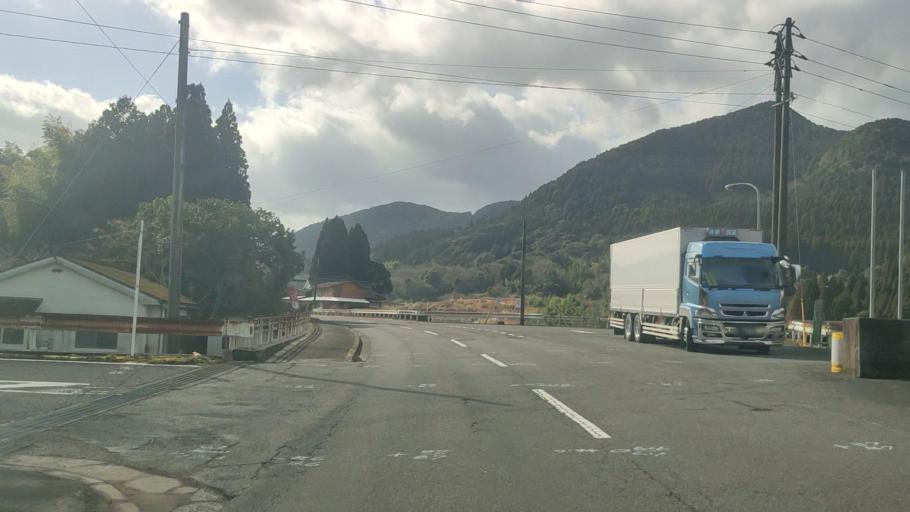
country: JP
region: Kagoshima
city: Okuchi-shinohara
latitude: 31.9896
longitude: 130.7450
